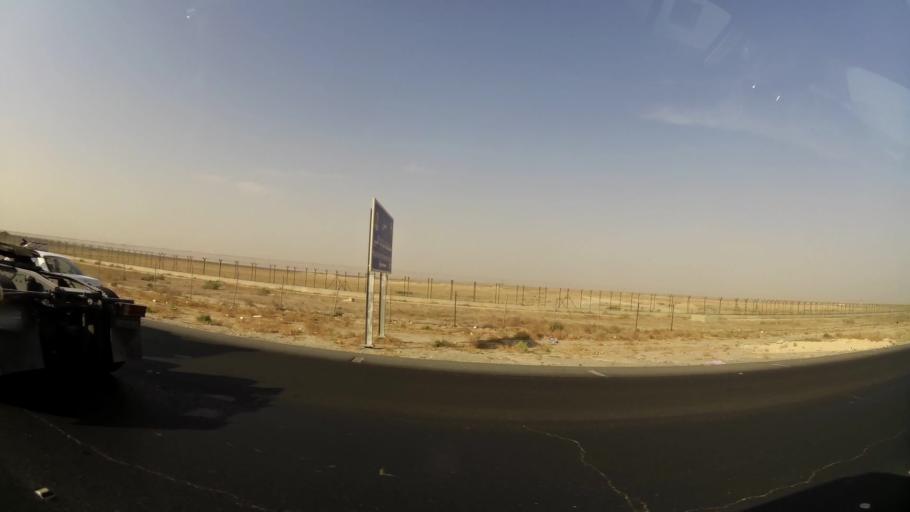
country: KW
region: Al Farwaniyah
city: Janub as Surrah
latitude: 29.2028
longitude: 48.0074
